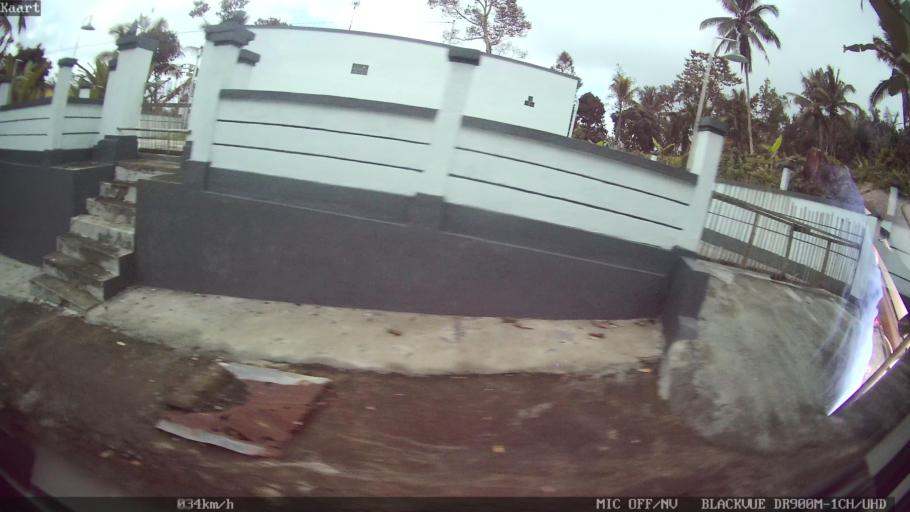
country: ID
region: Bali
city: Peneng
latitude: -8.3587
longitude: 115.2062
